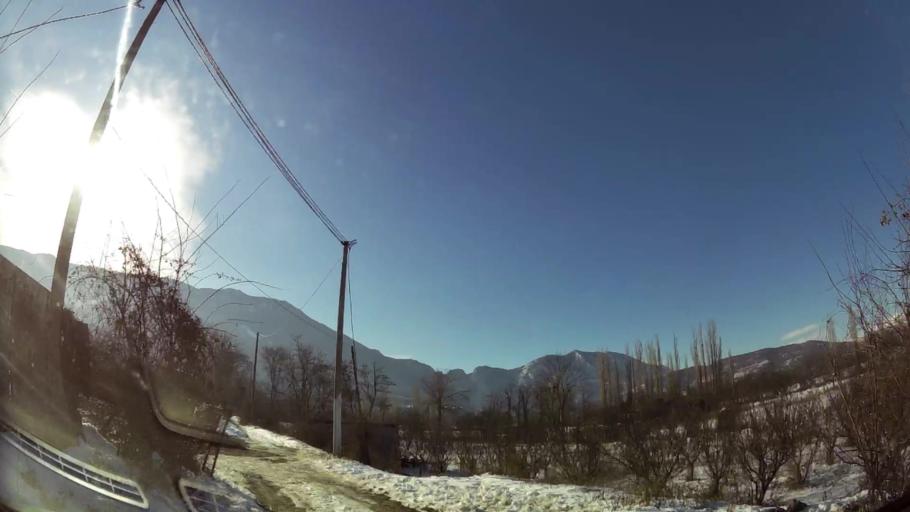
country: MK
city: Grchec
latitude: 41.9850
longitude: 21.3239
